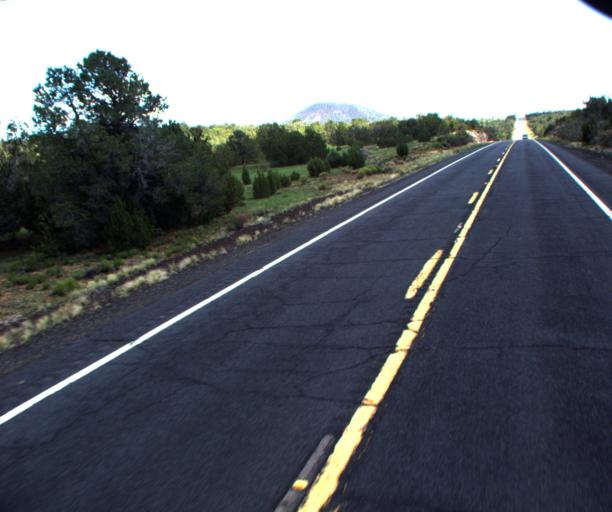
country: US
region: Arizona
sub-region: Coconino County
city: Williams
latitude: 35.4311
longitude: -112.1711
